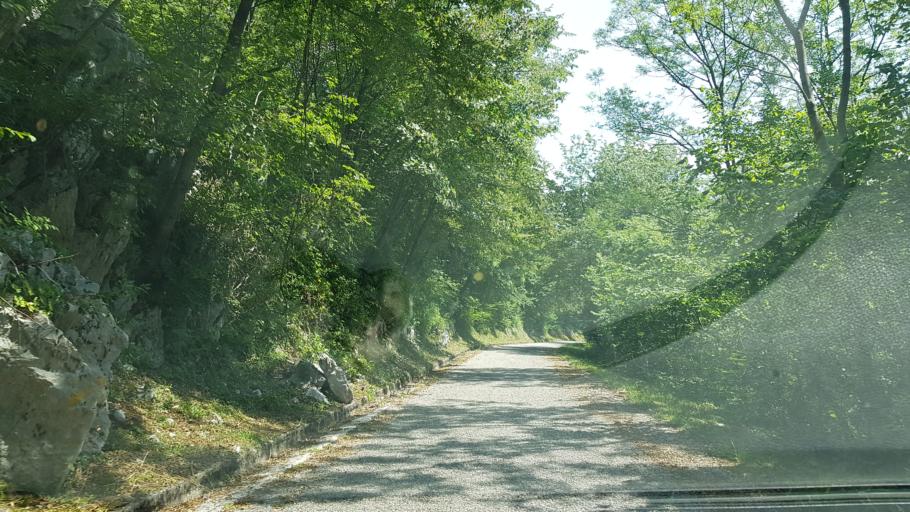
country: IT
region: Friuli Venezia Giulia
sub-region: Provincia di Udine
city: Nimis
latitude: 46.2372
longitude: 13.2581
